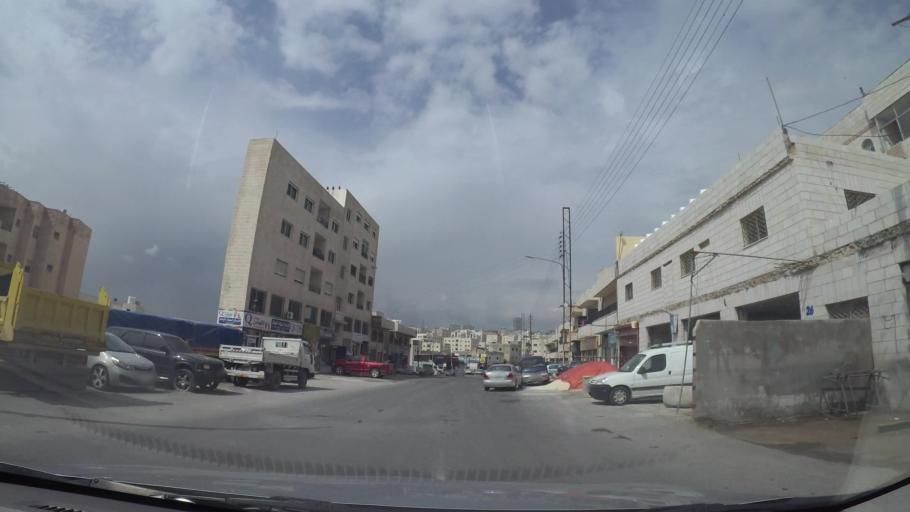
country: JO
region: Amman
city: Umm as Summaq
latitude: 31.8993
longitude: 35.8382
